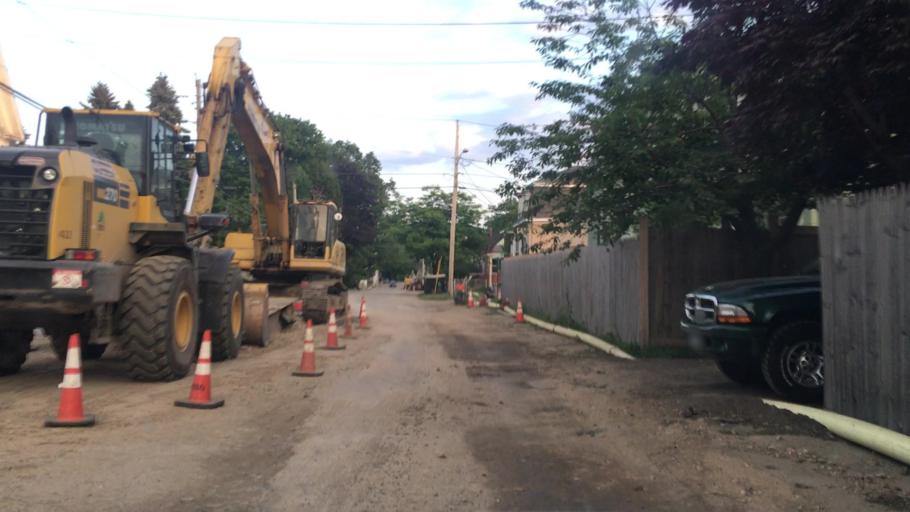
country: US
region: Maine
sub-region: Cumberland County
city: South Portland
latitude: 43.6333
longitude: -70.2686
